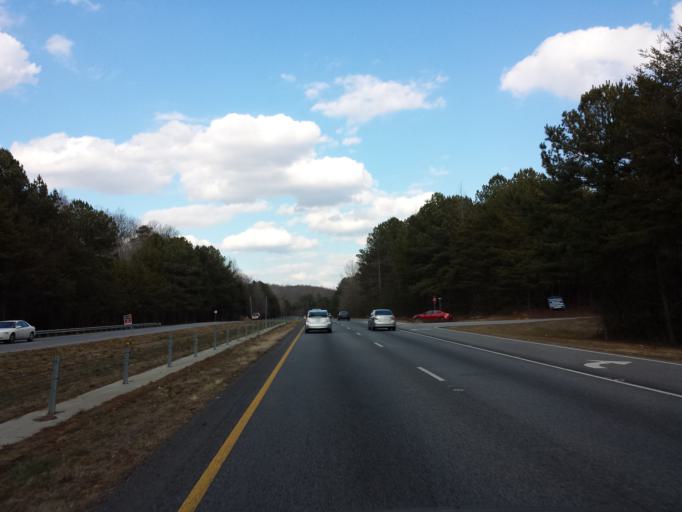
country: US
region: Georgia
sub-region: Dawson County
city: Dawsonville
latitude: 34.3909
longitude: -84.0203
